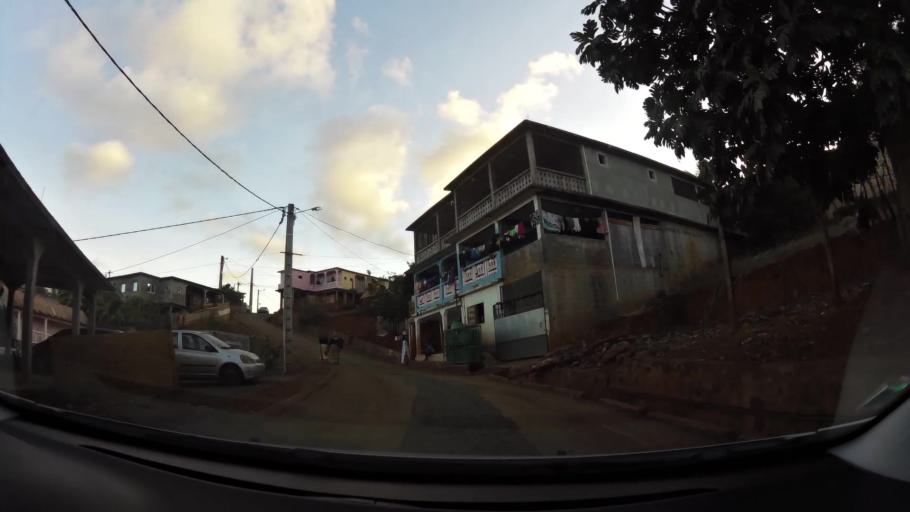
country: YT
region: Dembeni
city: Dembeni
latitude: -12.8672
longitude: 45.1962
